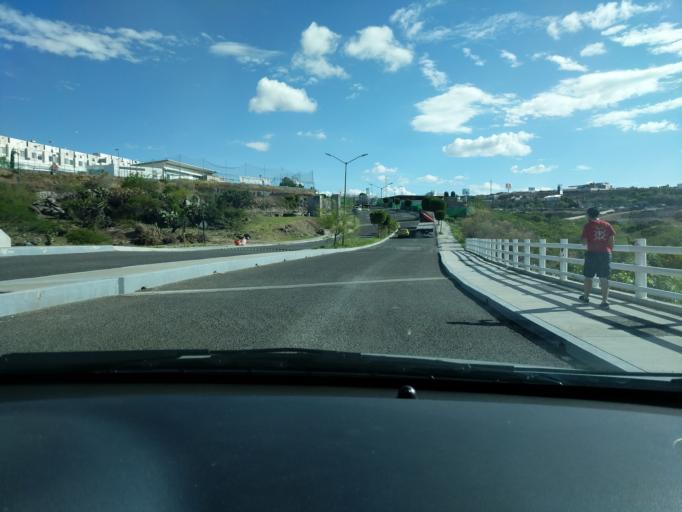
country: MX
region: Queretaro
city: La Canada
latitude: 20.5880
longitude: -100.3374
